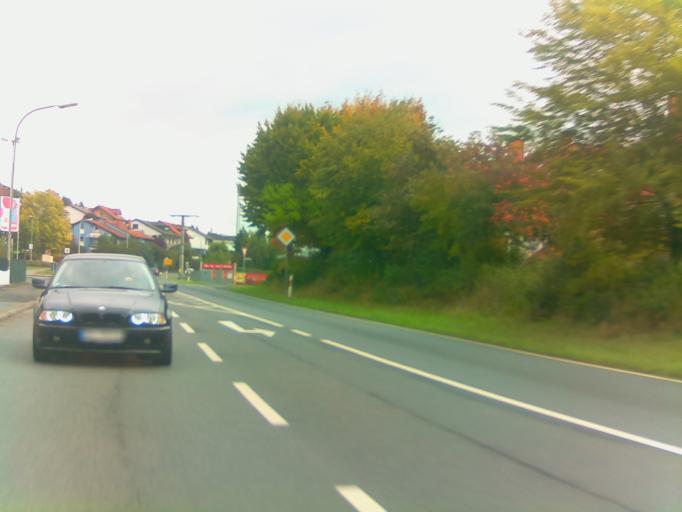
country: DE
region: Bavaria
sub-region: Regierungsbezirk Unterfranken
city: Obernburg am Main
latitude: 49.8358
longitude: 9.1159
